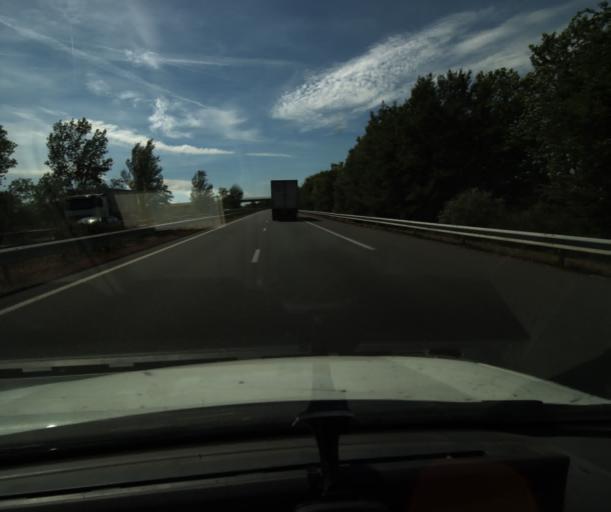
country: FR
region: Midi-Pyrenees
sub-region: Departement du Tarn-et-Garonne
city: Saint-Porquier
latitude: 44.0164
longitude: 1.1930
